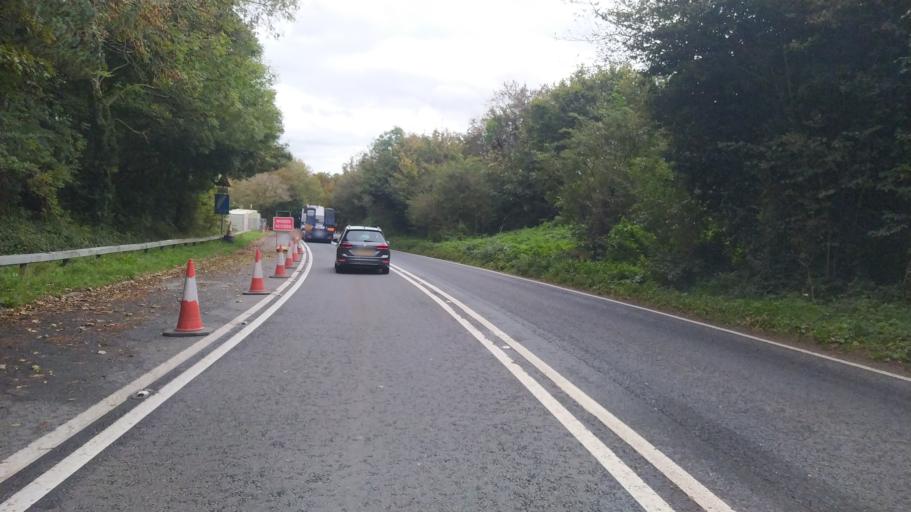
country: GB
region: England
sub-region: Dorset
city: Bridport
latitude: 50.7367
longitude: -2.8331
